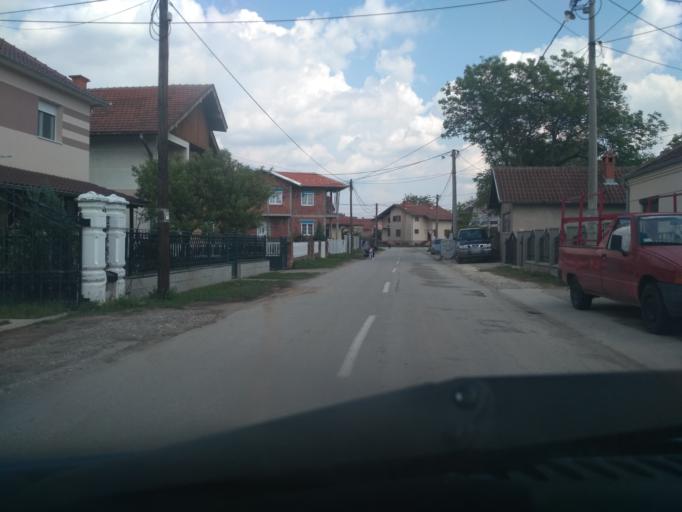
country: RS
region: Central Serbia
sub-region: Pomoravski Okrug
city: Svilajnac
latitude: 44.2348
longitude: 21.2027
